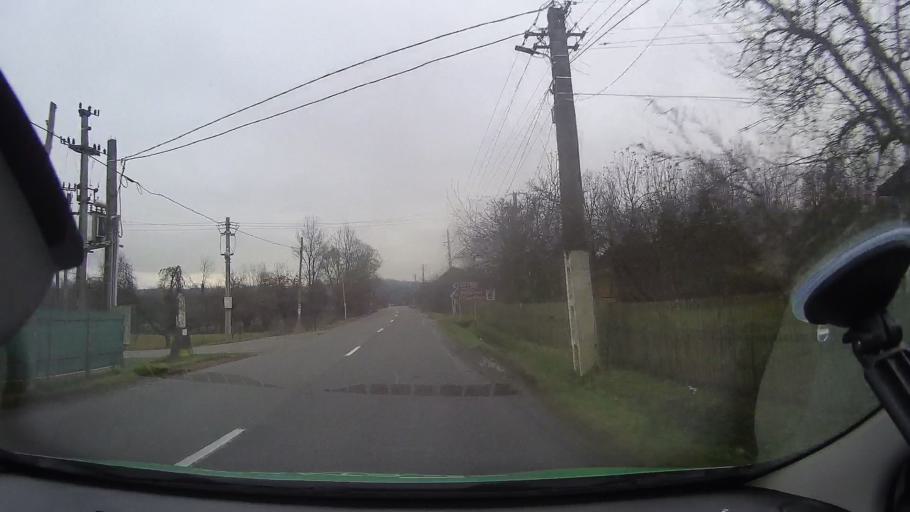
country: RO
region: Arad
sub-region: Comuna Varfurile
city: Varfurile
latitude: 46.3132
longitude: 22.5139
